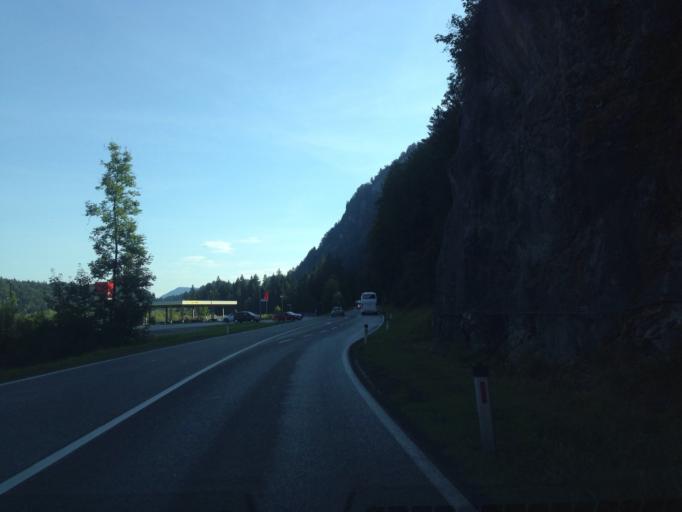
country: AT
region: Tyrol
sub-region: Politischer Bezirk Reutte
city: Musau
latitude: 47.5507
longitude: 10.6688
